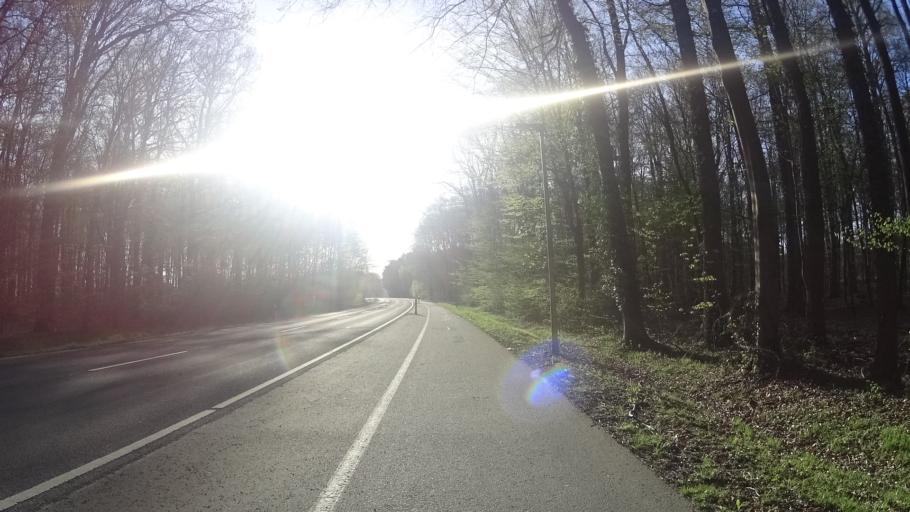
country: DE
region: North Rhine-Westphalia
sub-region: Regierungsbezirk Munster
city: Greven
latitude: 52.1135
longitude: 7.5682
